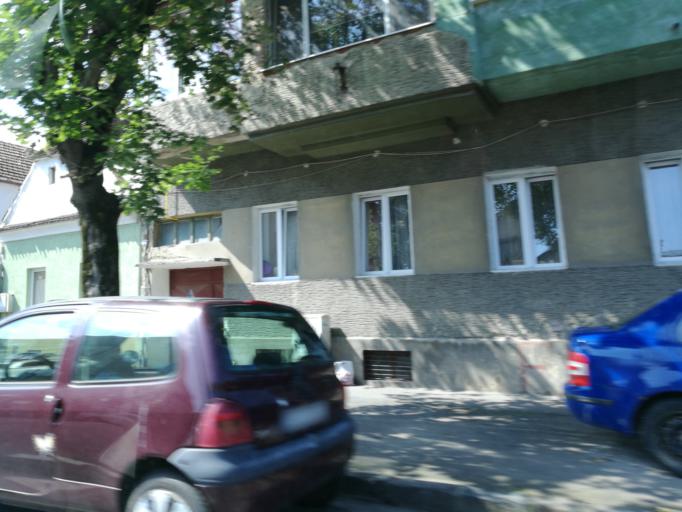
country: RO
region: Brasov
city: Brasov
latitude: 45.6563
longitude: 25.5898
